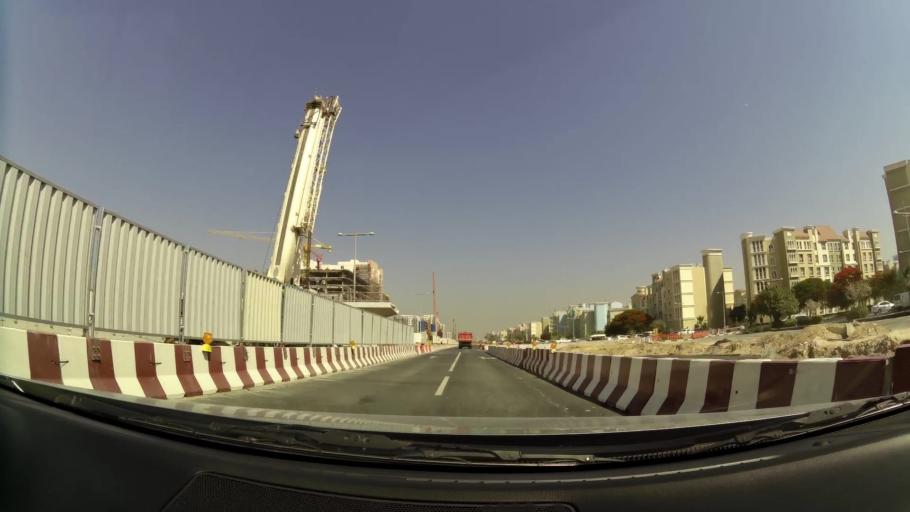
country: AE
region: Dubai
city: Dubai
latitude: 25.0273
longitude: 55.1558
